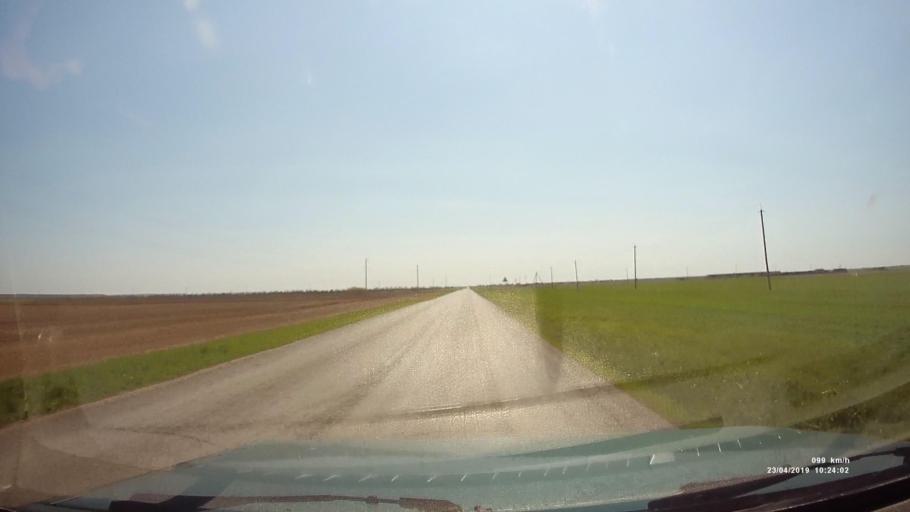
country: RU
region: Rostov
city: Sovetskoye
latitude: 46.6424
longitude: 42.4346
